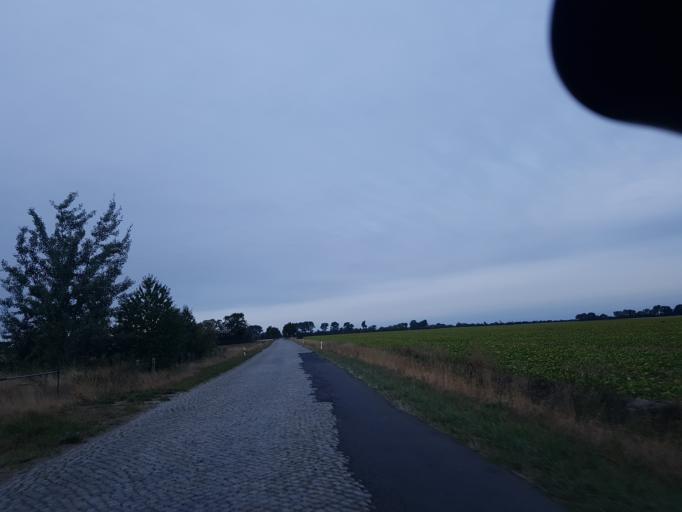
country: DE
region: Brandenburg
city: Muhlberg
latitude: 51.4971
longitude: 13.2262
